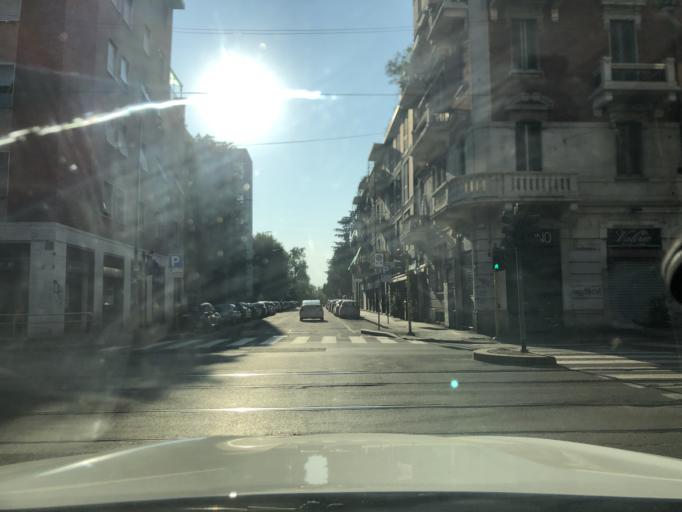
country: IT
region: Lombardy
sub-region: Citta metropolitana di Milano
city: Milano
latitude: 45.4914
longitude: 9.1844
